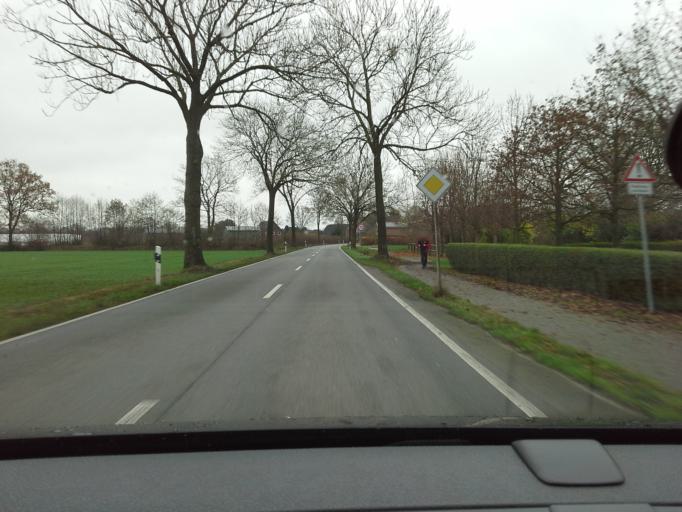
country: DE
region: Schleswig-Holstein
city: Hemdingen
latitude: 53.7635
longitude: 9.8533
